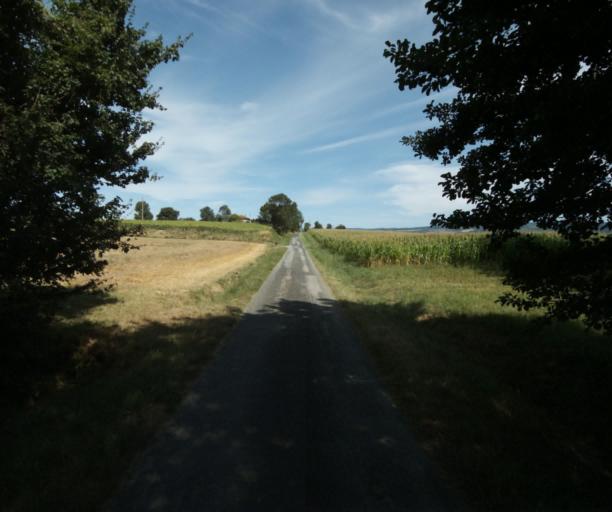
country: FR
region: Midi-Pyrenees
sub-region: Departement du Tarn
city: Soreze
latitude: 43.5121
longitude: 2.0699
